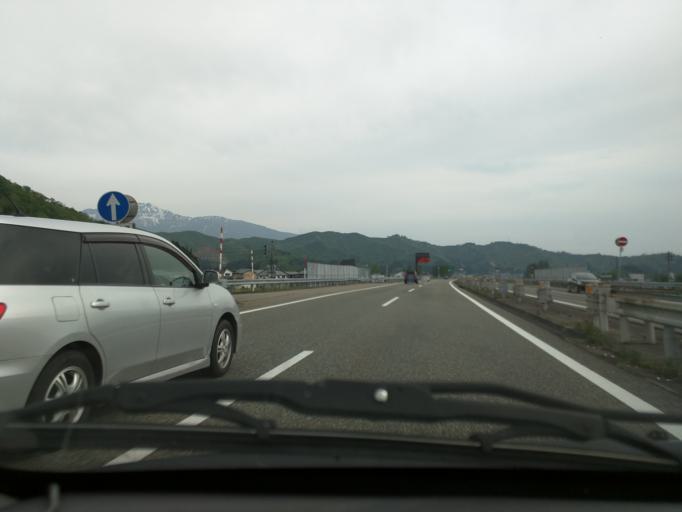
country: JP
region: Niigata
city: Muikamachi
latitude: 37.2214
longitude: 138.9770
